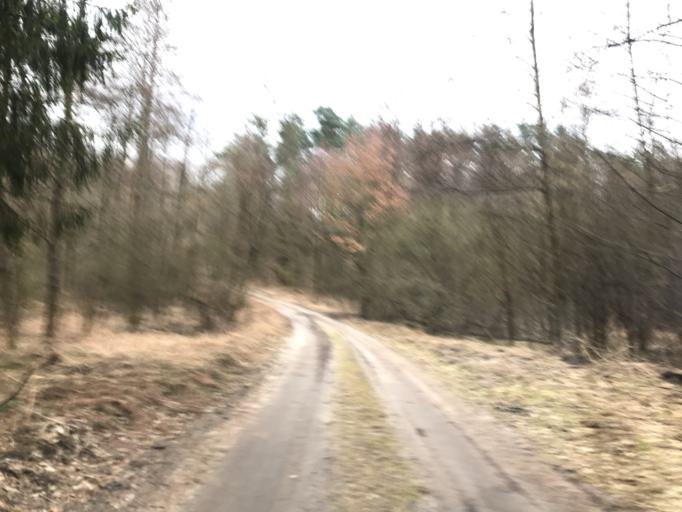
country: PL
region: Kujawsko-Pomorskie
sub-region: Powiat brodnicki
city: Gorzno
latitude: 53.2243
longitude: 19.6618
